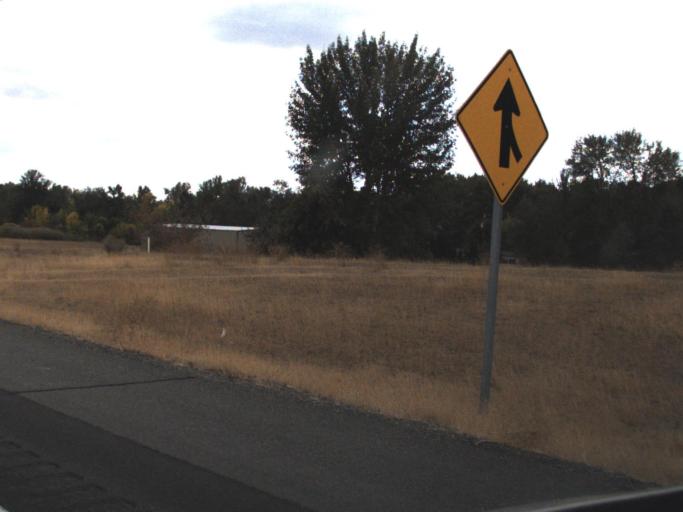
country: US
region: Washington
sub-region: Yakima County
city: Wapato
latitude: 46.4696
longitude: -120.3938
